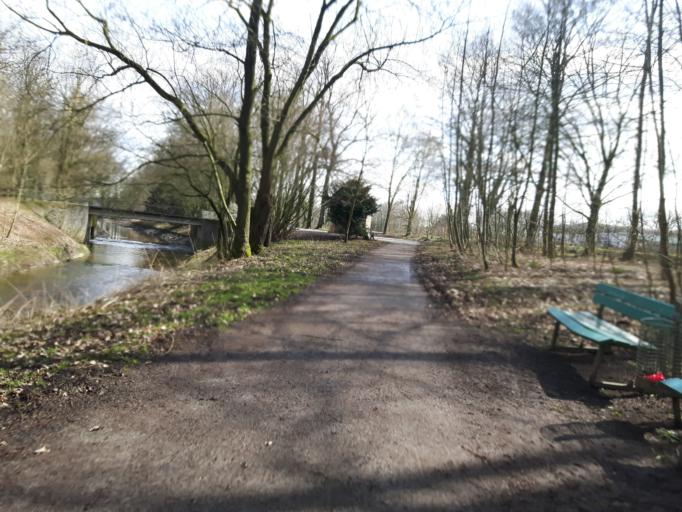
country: DE
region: North Rhine-Westphalia
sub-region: Regierungsbezirk Munster
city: Senden
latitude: 51.8500
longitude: 7.4747
